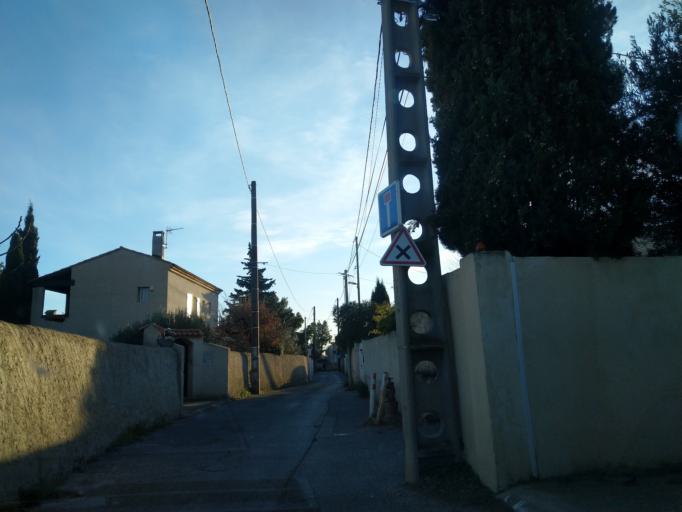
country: FR
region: Provence-Alpes-Cote d'Azur
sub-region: Departement des Bouches-du-Rhone
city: Plan-de-Cuques
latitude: 43.3544
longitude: 5.4592
